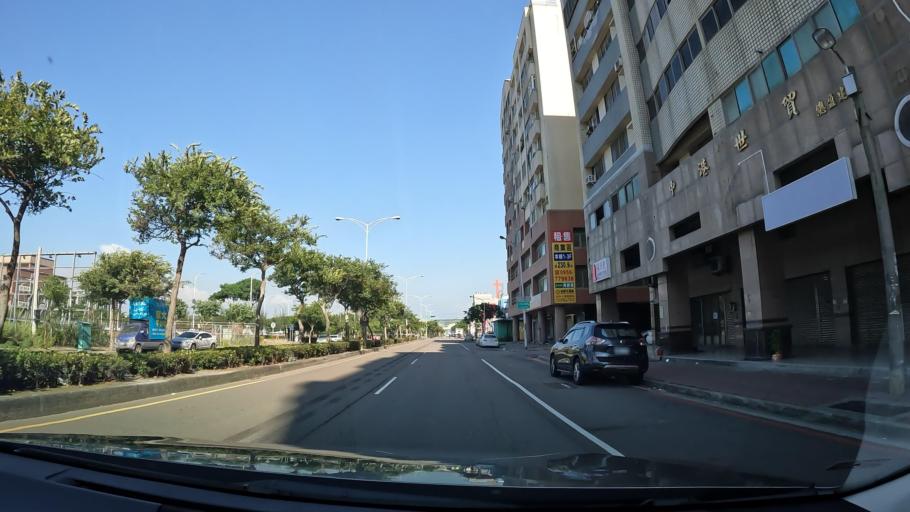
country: TW
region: Taiwan
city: Fengyuan
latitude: 24.2637
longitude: 120.5337
